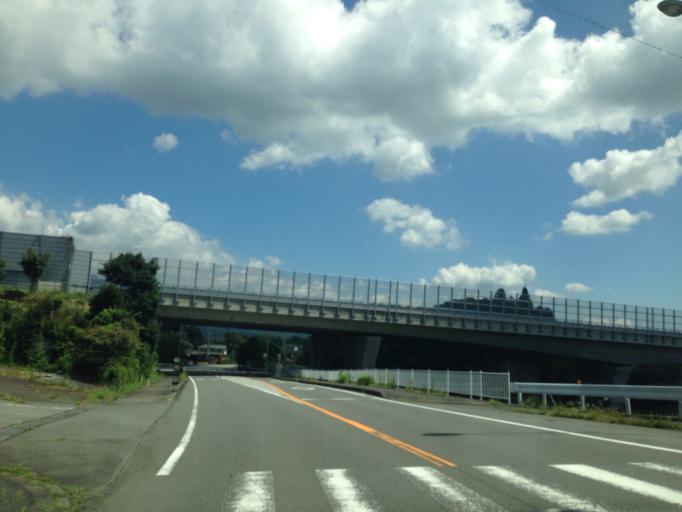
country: JP
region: Shizuoka
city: Gotemba
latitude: 35.2220
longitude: 138.8874
